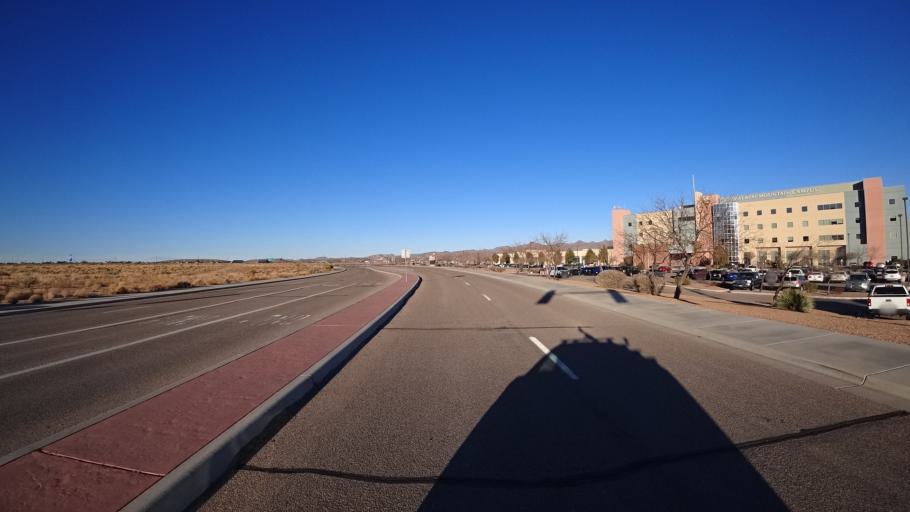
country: US
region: Arizona
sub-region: Mohave County
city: New Kingman-Butler
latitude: 35.2181
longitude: -113.9842
